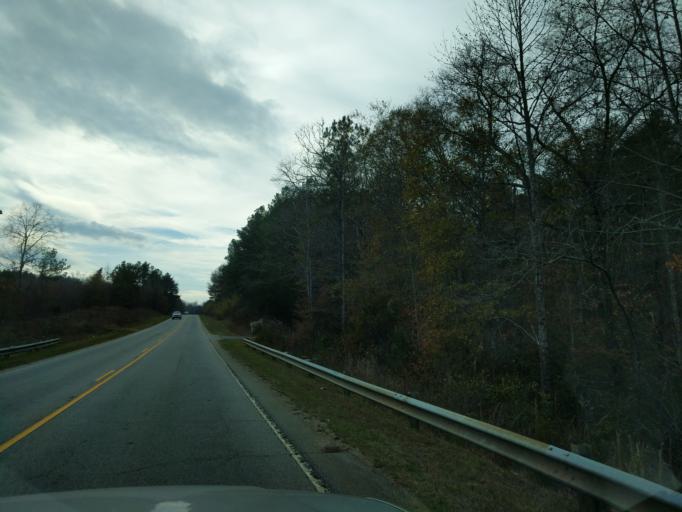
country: US
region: South Carolina
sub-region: Oconee County
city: Utica
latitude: 34.7622
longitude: -82.8997
